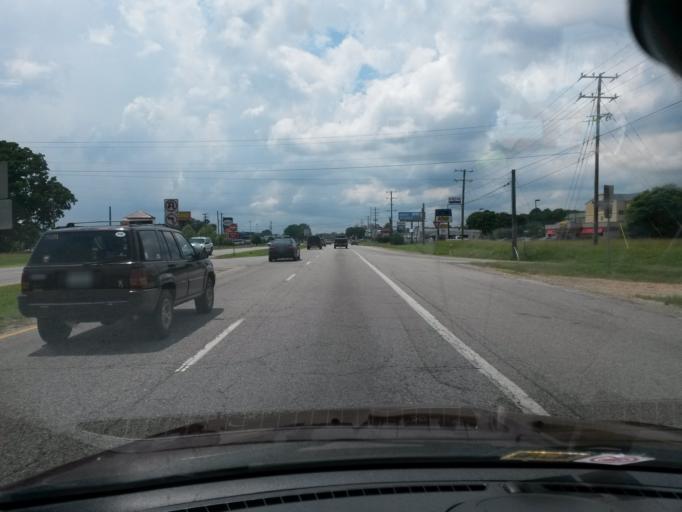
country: US
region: Virginia
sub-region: Chesterfield County
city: Chester
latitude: 37.3548
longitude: -77.4065
